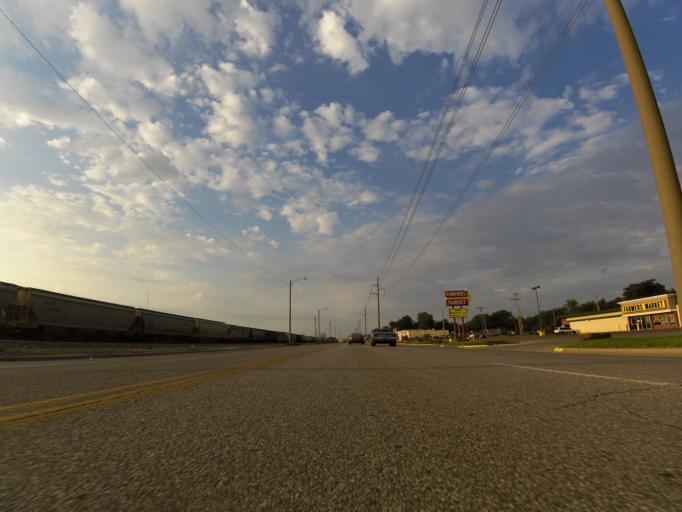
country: US
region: Kansas
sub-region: Sedgwick County
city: Wichita
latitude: 37.7365
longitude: -97.3359
